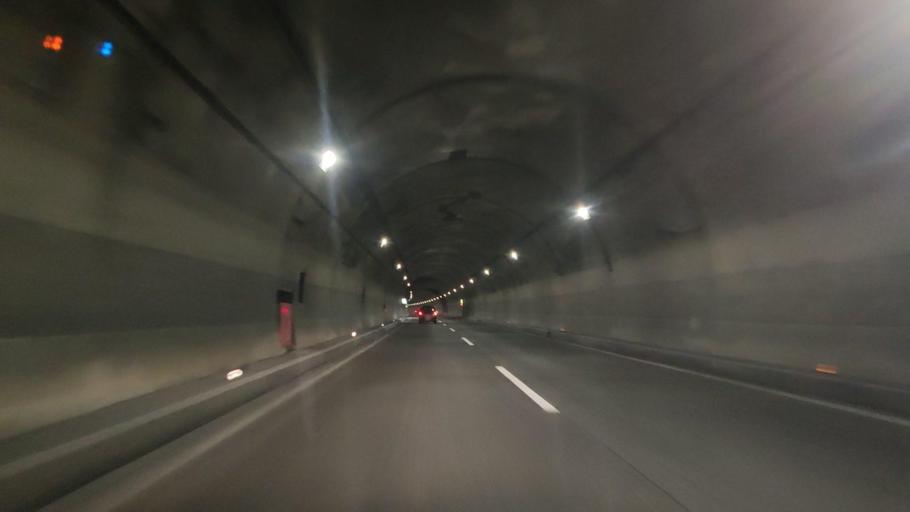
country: JP
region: Oita
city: Beppu
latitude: 33.2726
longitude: 131.3423
